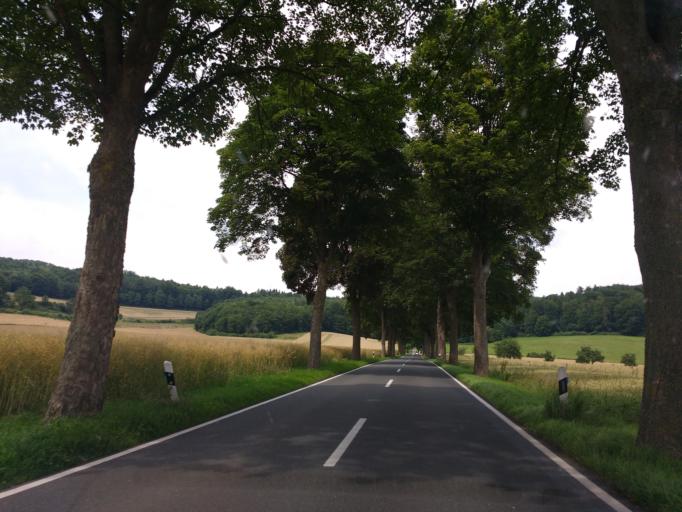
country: DE
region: Lower Saxony
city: Bad Pyrmont
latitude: 51.9943
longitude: 9.2169
